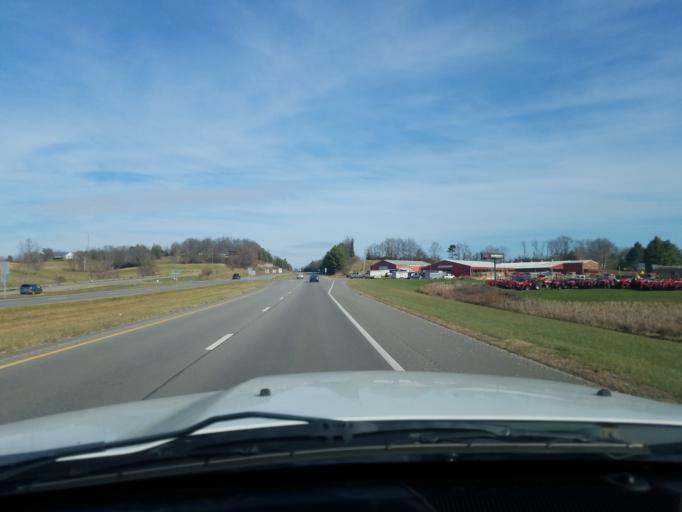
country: US
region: Ohio
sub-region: Athens County
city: Athens
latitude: 39.2518
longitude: -82.1767
